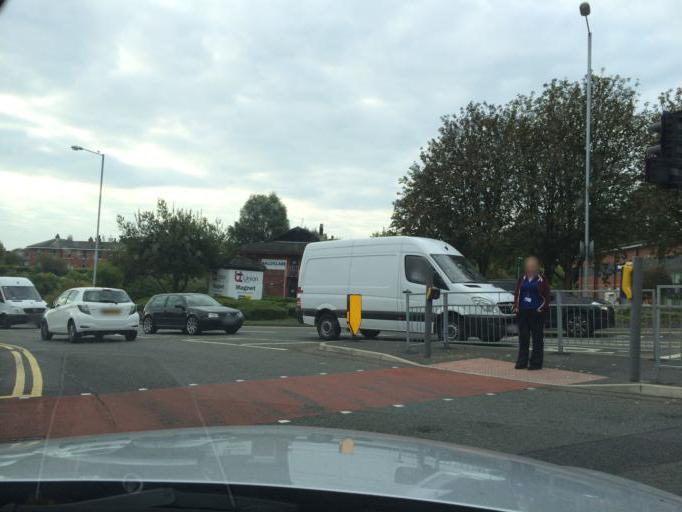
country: GB
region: England
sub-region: Borough of Stockport
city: Stockport
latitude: 53.4028
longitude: -2.1496
